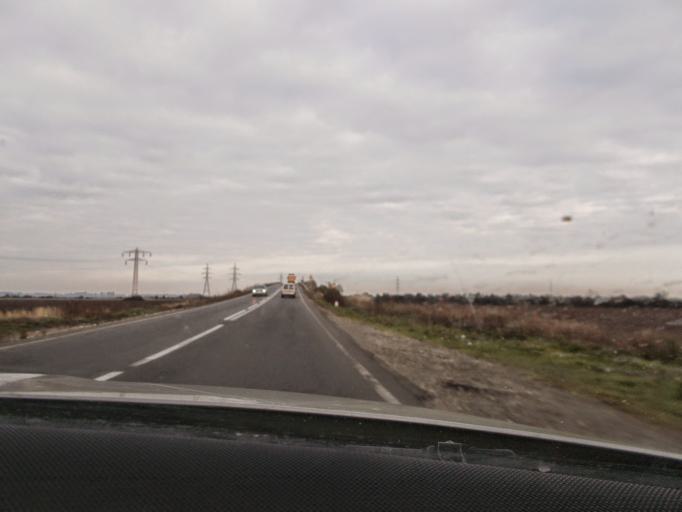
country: RO
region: Dambovita
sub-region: Comuna Racari
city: Mavrodin
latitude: 44.6463
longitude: 25.6991
